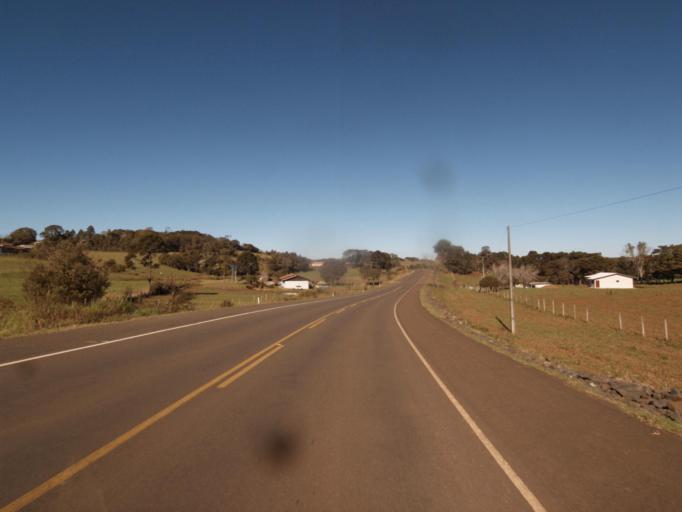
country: AR
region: Misiones
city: Bernardo de Irigoyen
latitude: -26.6717
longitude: -53.5705
